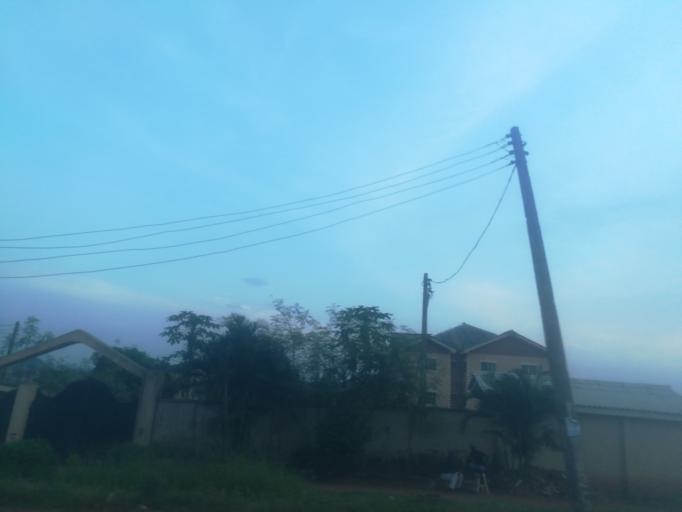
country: NG
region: Ogun
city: Abeokuta
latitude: 7.1763
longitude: 3.3874
